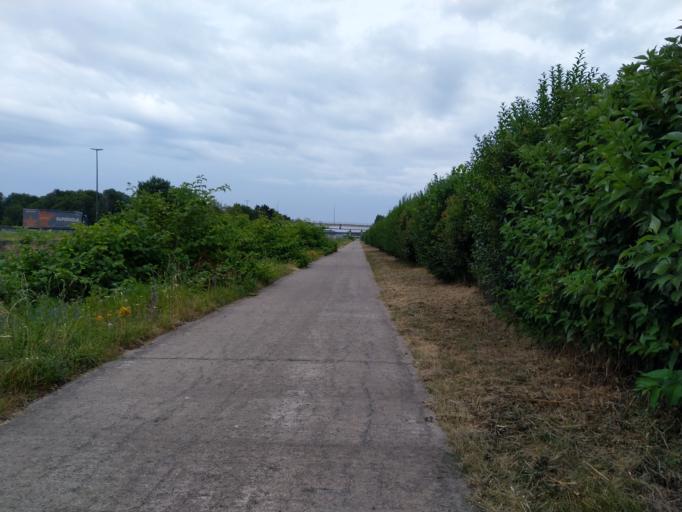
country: BE
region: Wallonia
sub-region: Province du Hainaut
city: Boussu
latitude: 50.4524
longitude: 3.7925
